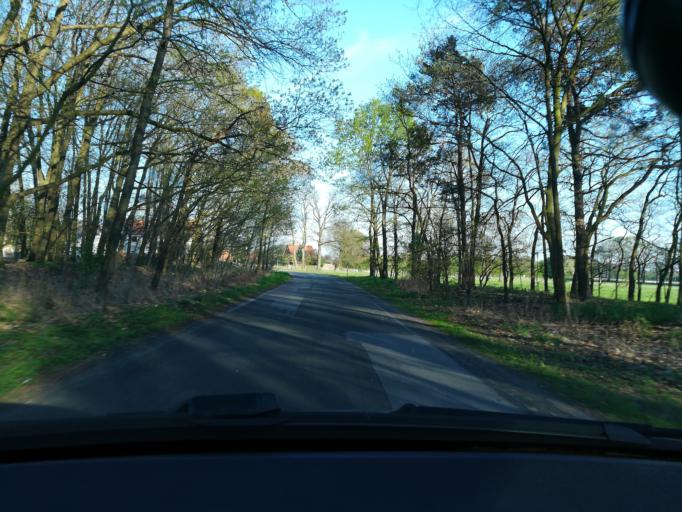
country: DE
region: North Rhine-Westphalia
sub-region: Regierungsbezirk Munster
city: Sassenberg
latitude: 52.0276
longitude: 8.0872
